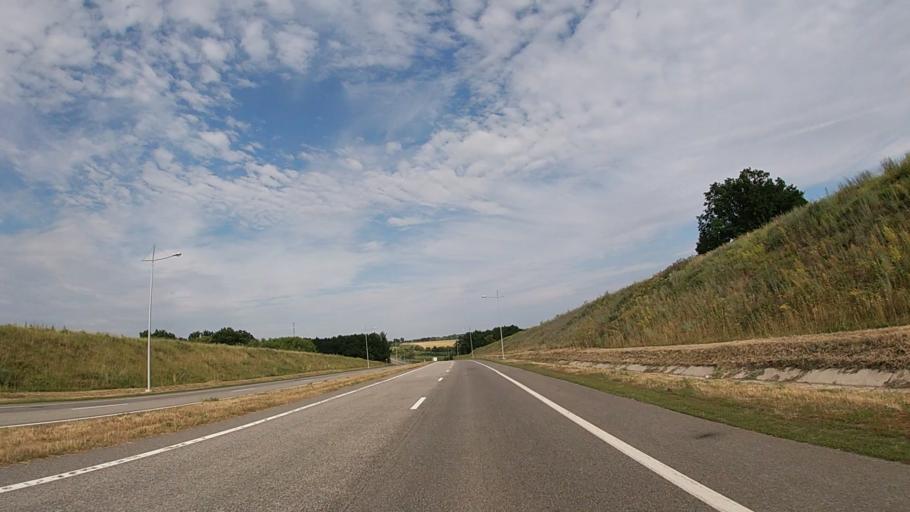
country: RU
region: Belgorod
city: Tomarovka
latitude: 50.7067
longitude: 36.2118
